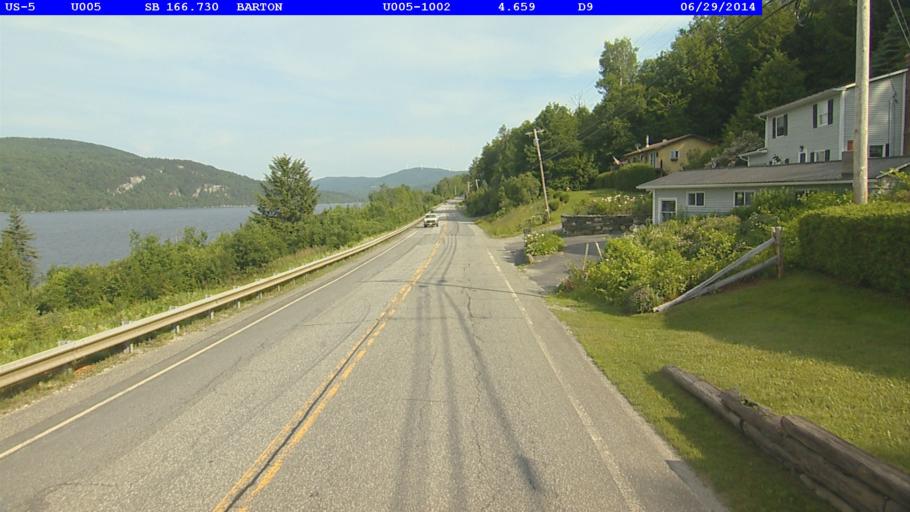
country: US
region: Vermont
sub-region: Orleans County
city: Newport
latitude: 44.7395
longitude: -72.1676
